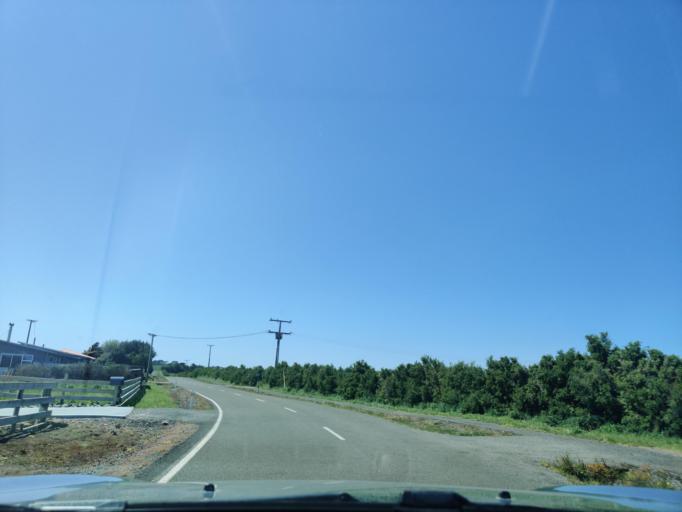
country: NZ
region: Taranaki
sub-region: South Taranaki District
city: Hawera
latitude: -39.6039
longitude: 174.2446
